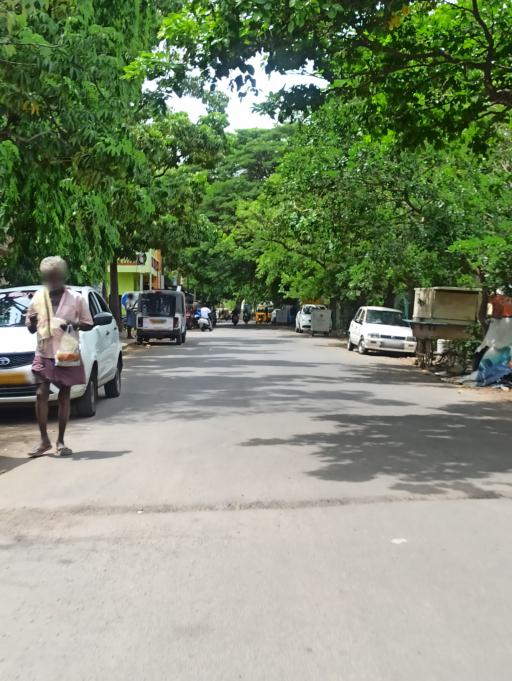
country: IN
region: Tamil Nadu
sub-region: Chennai
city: Chetput
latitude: 13.0564
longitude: 80.2260
